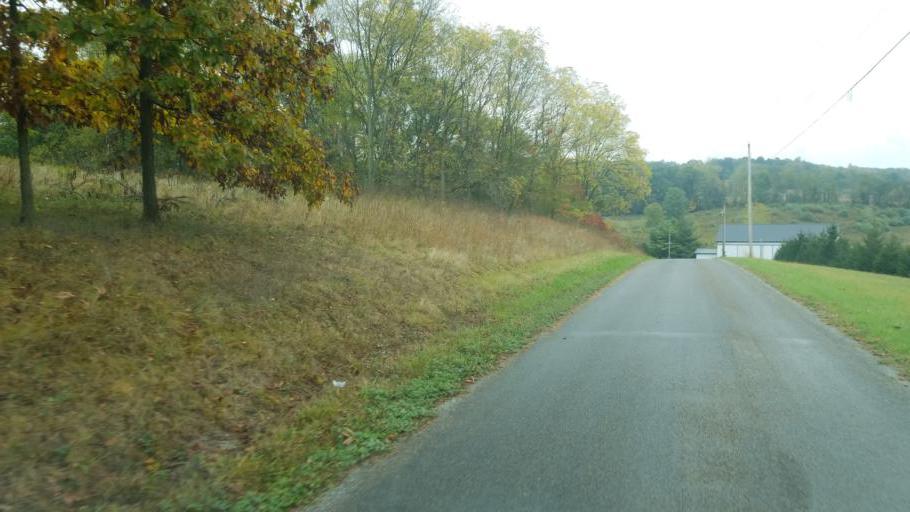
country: US
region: Ohio
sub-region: Knox County
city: Danville
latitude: 40.5152
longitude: -82.3277
